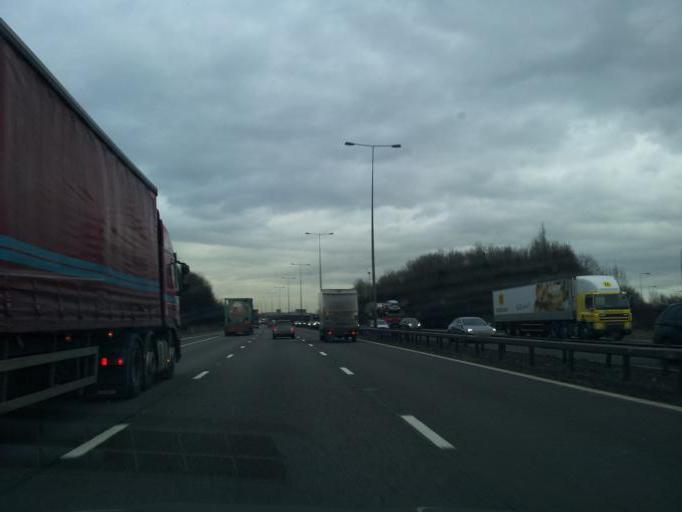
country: GB
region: England
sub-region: Warwickshire
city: Brandon
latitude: 52.4372
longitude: -1.4203
